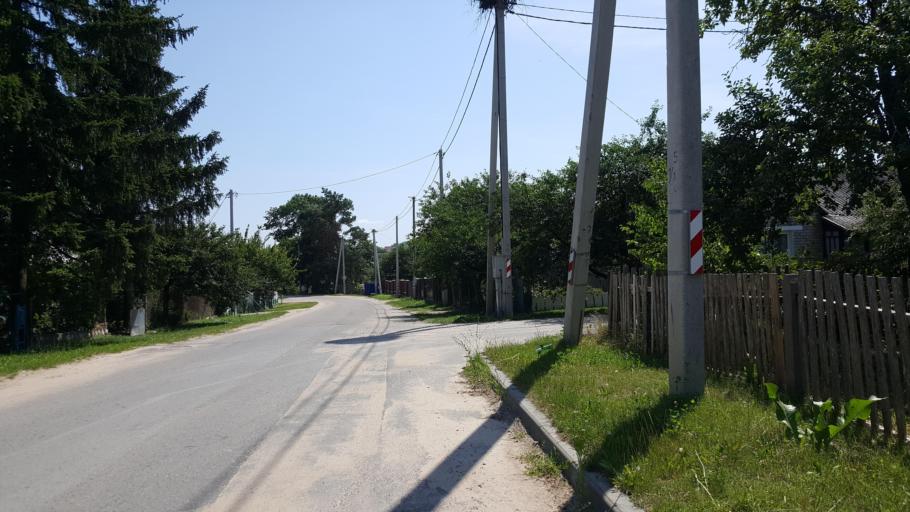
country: BY
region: Brest
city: Vysokaye
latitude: 52.3622
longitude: 23.3827
